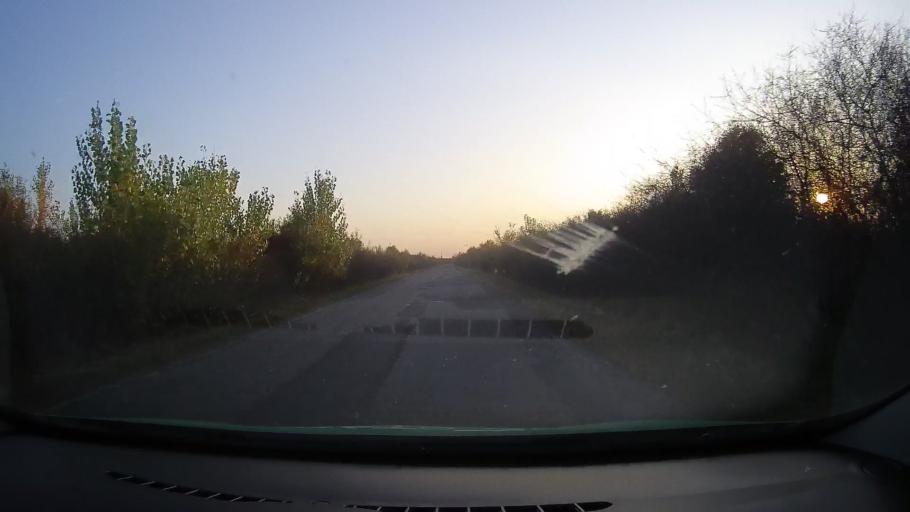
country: RO
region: Arad
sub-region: Comuna Seleus
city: Seleus
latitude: 46.4066
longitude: 21.7298
